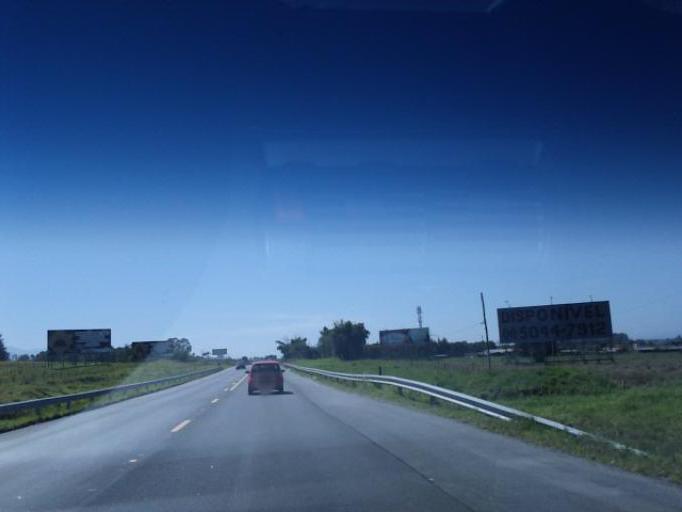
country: BR
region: Sao Paulo
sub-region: Tremembe
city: Tremembe
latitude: -22.9478
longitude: -45.6111
